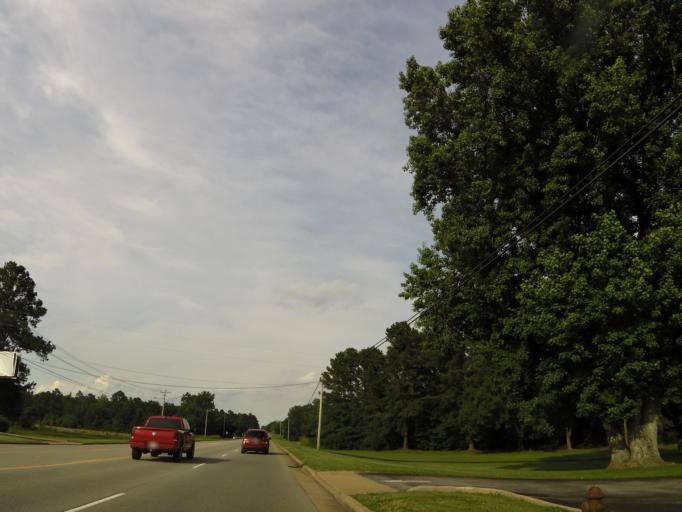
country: US
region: Tennessee
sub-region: Humphreys County
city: Johnsonville
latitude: 36.0352
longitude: -87.9391
